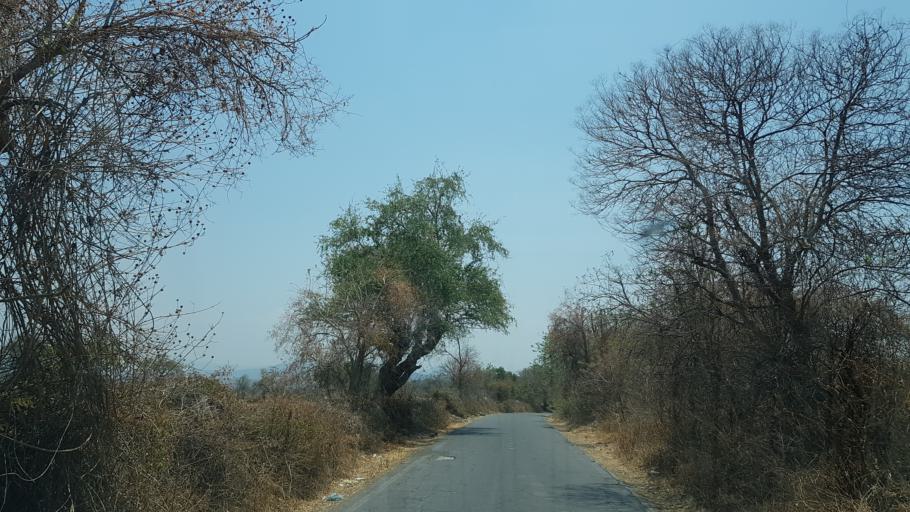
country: MX
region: Puebla
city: Huaquechula
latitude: 18.7835
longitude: -98.5453
